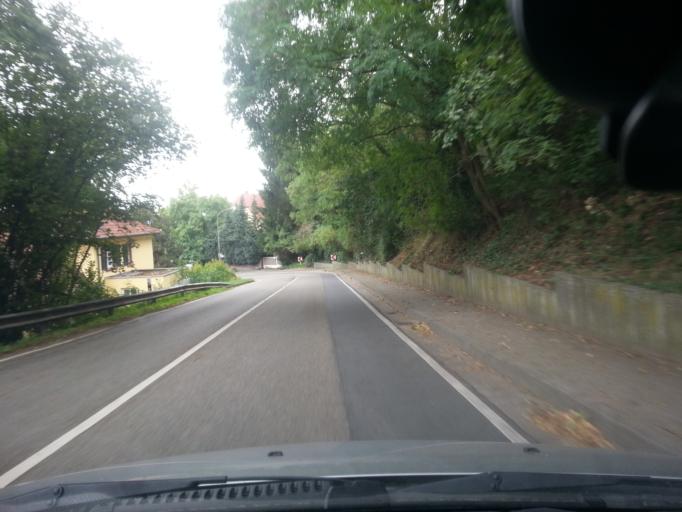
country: DE
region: Rheinland-Pfalz
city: Neuleiningen
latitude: 49.5435
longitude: 8.1401
